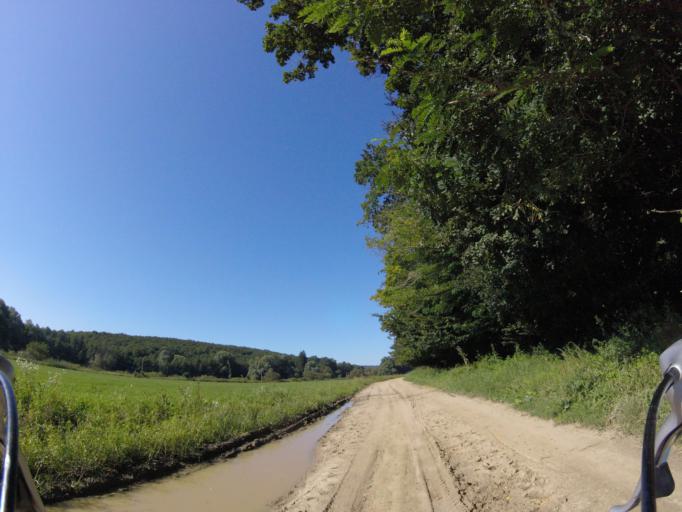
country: HU
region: Zala
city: Becsehely
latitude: 46.5507
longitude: 16.7481
